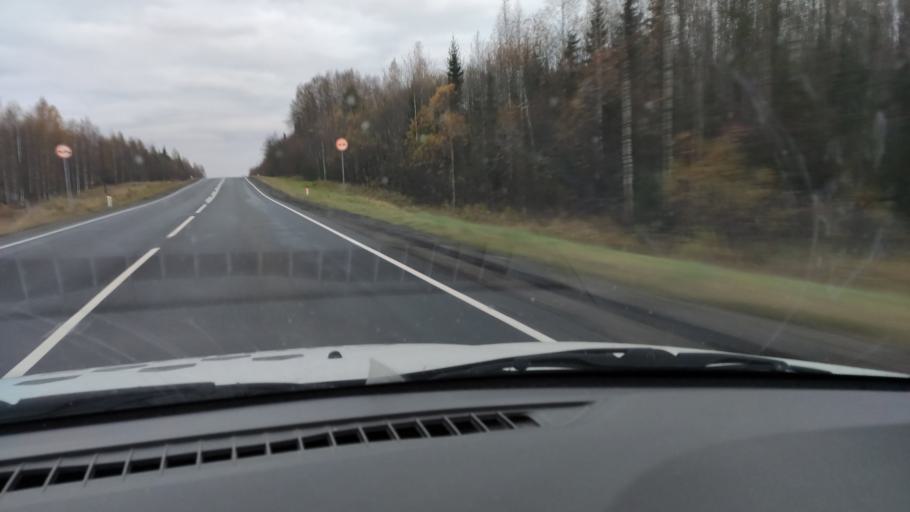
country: RU
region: Kirov
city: Lesnyye Polyany
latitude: 58.8015
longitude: 52.5666
